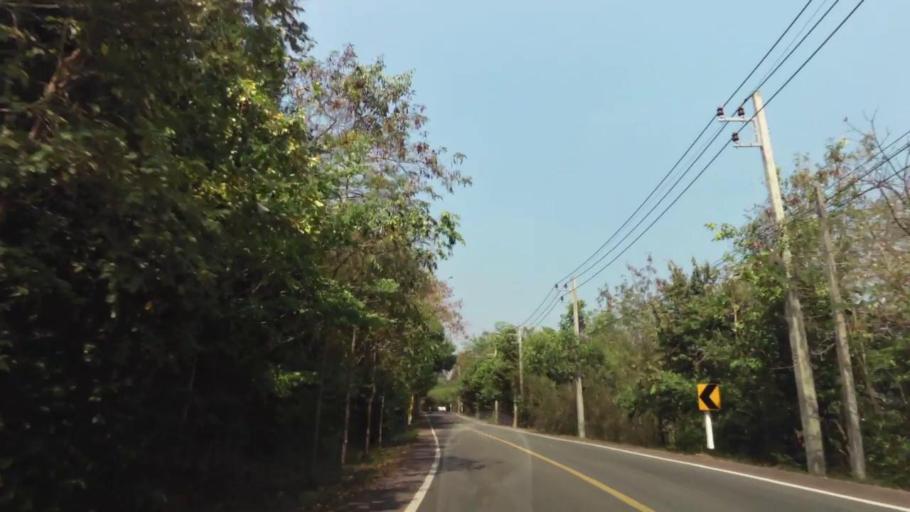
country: TH
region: Chanthaburi
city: Tha Mai
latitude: 12.5369
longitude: 101.9471
